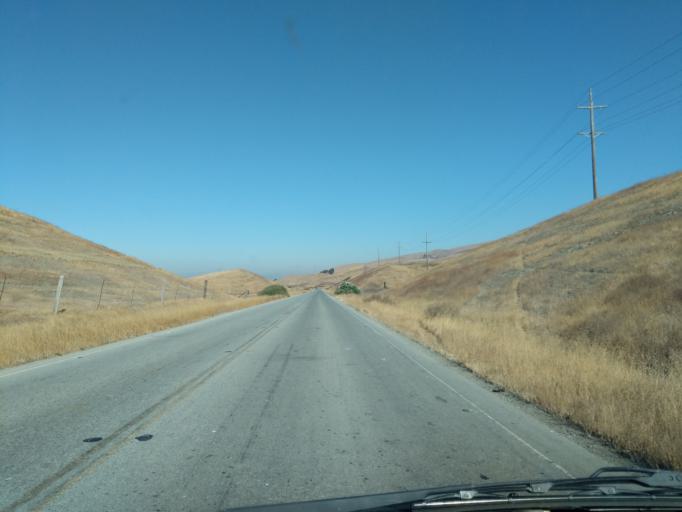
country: US
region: California
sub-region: Santa Clara County
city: Morgan Hill
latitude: 37.1862
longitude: -121.6834
